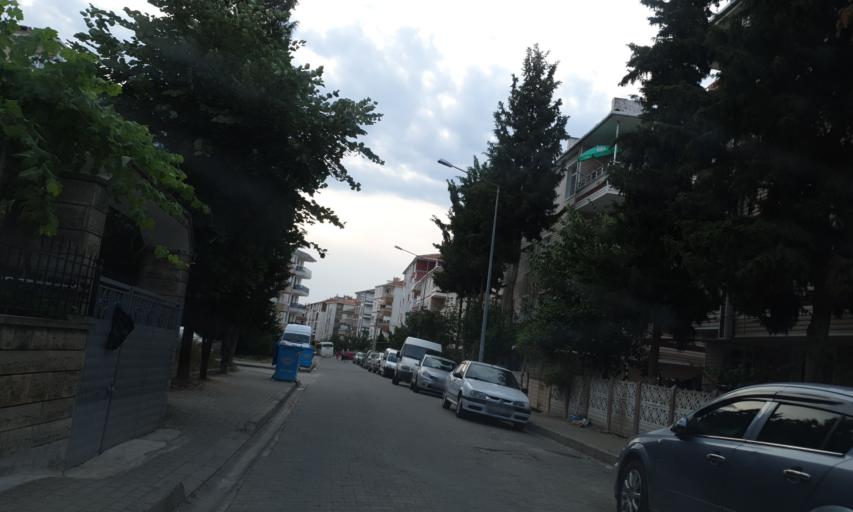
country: TR
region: Kirklareli
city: Luleburgaz
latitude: 41.4045
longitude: 27.3656
